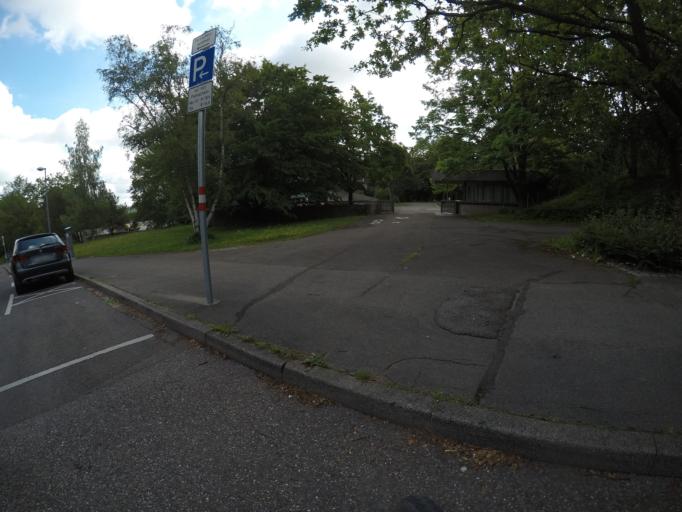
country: DE
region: Baden-Wuerttemberg
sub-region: Regierungsbezirk Stuttgart
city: Ostfildern
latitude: 48.7416
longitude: 9.2192
